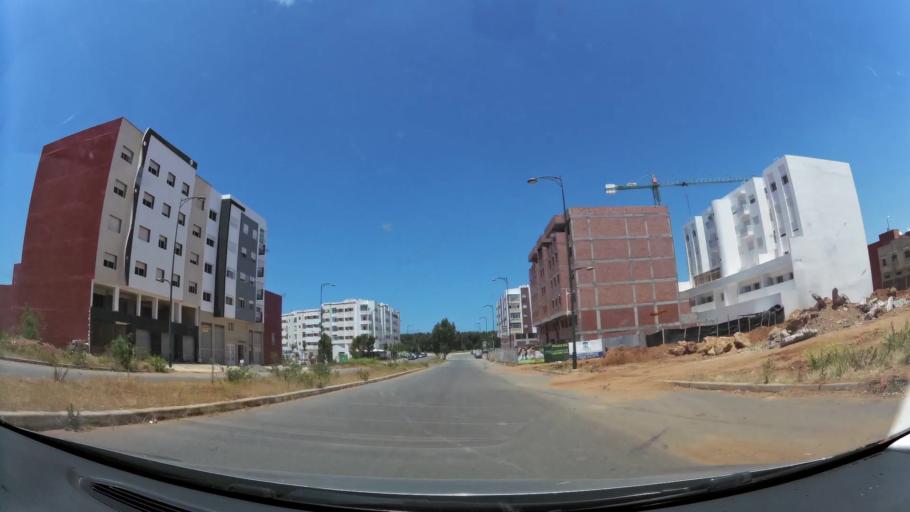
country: MA
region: Gharb-Chrarda-Beni Hssen
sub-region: Kenitra Province
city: Kenitra
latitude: 34.2696
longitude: -6.6276
